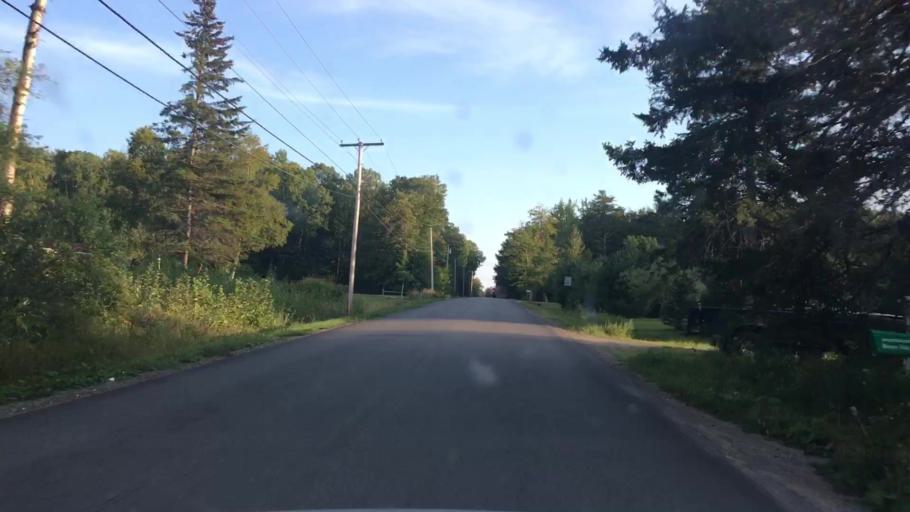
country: US
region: Maine
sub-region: Penobscot County
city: Hampden
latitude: 44.7190
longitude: -68.8870
